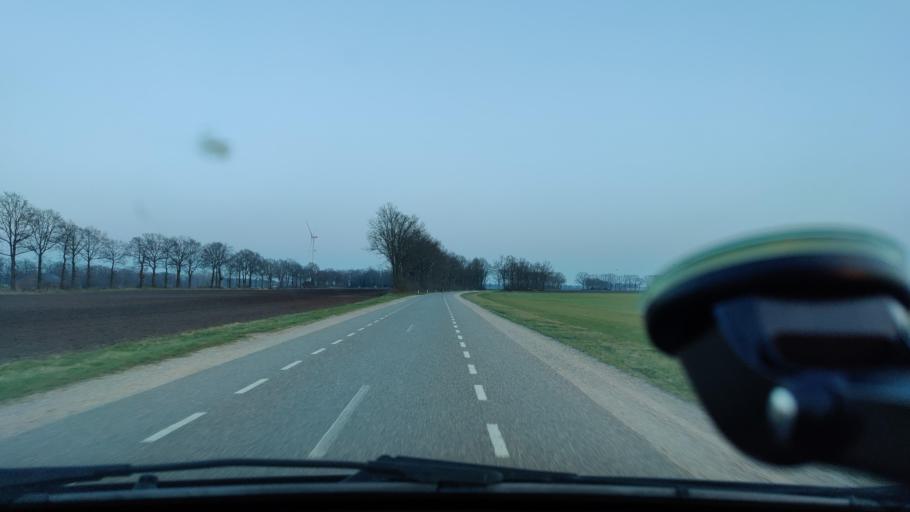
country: NL
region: Limburg
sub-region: Gemeente Bergen
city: Wellerlooi
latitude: 51.5711
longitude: 6.1399
